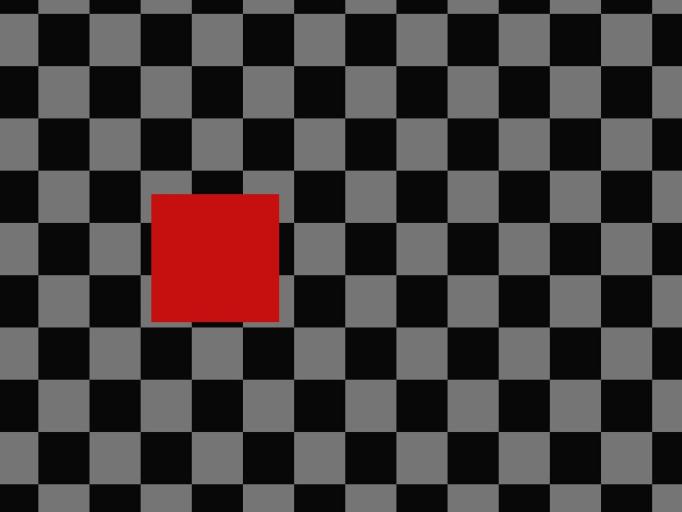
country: RO
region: Ilfov
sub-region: Comuna Popesti-Leordeni
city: Popesti-Leordeni
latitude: 44.4168
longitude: 26.1562
